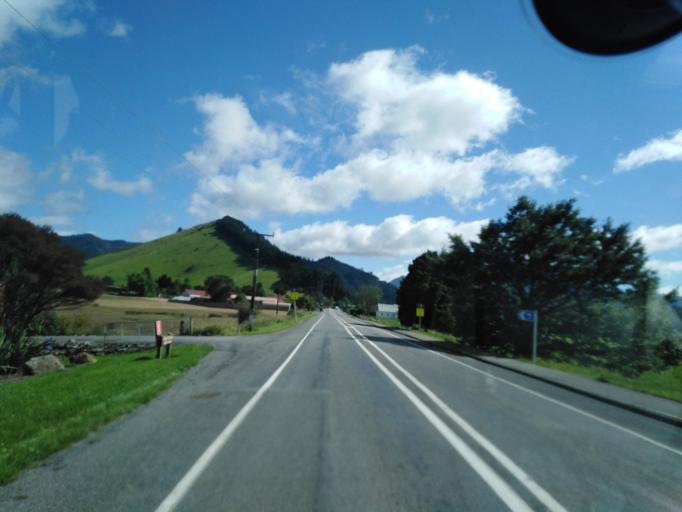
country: NZ
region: Nelson
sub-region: Nelson City
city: Nelson
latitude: -41.2323
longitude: 173.5816
